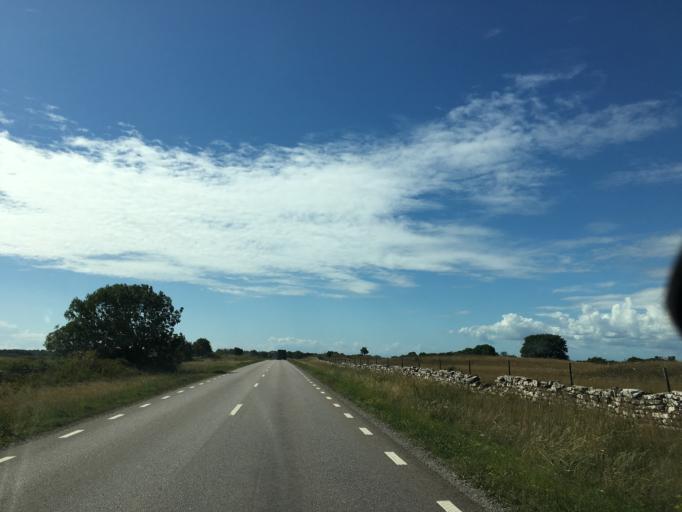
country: SE
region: Kalmar
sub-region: Morbylanga Kommun
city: Moerbylanga
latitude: 56.5324
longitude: 16.4431
